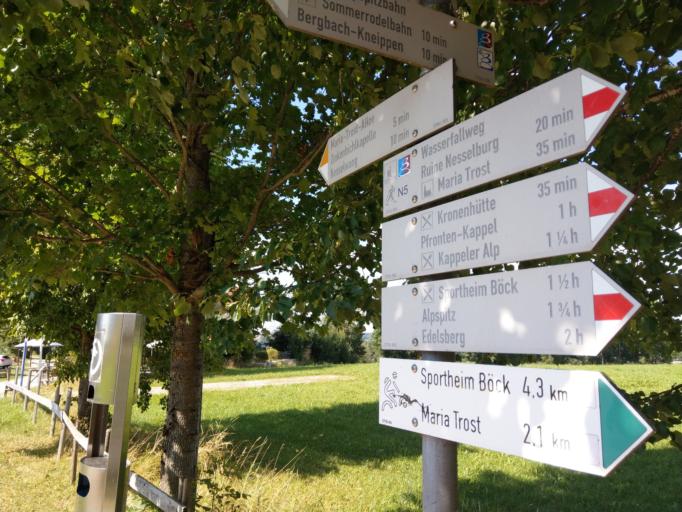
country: DE
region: Bavaria
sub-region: Swabia
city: Nesselwang
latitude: 47.6176
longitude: 10.5019
